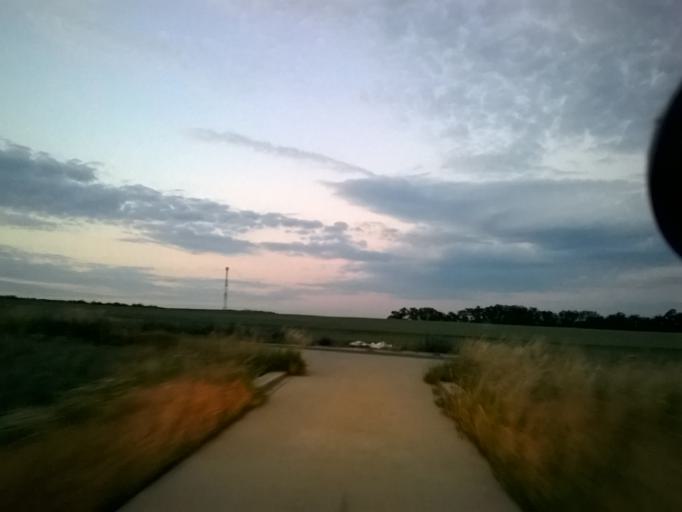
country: SK
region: Trnavsky
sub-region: Okres Senica
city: Senica
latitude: 48.7382
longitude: 17.3310
